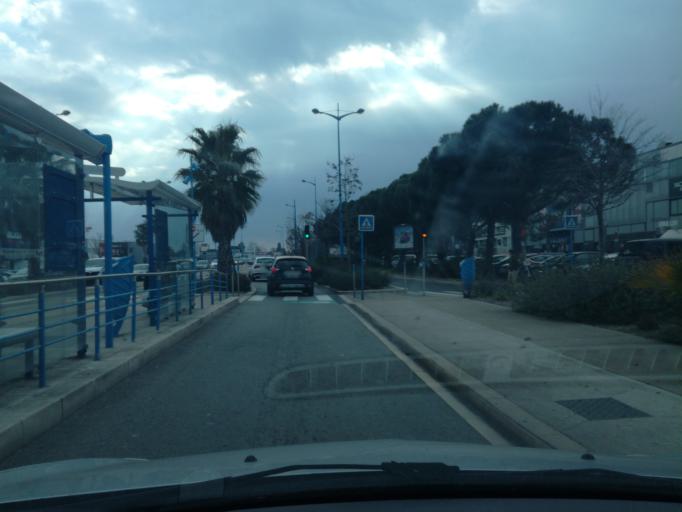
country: FR
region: Provence-Alpes-Cote d'Azur
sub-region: Departement des Alpes-Maritimes
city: Mandelieu-la-Napoule
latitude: 43.5547
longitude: 6.9543
